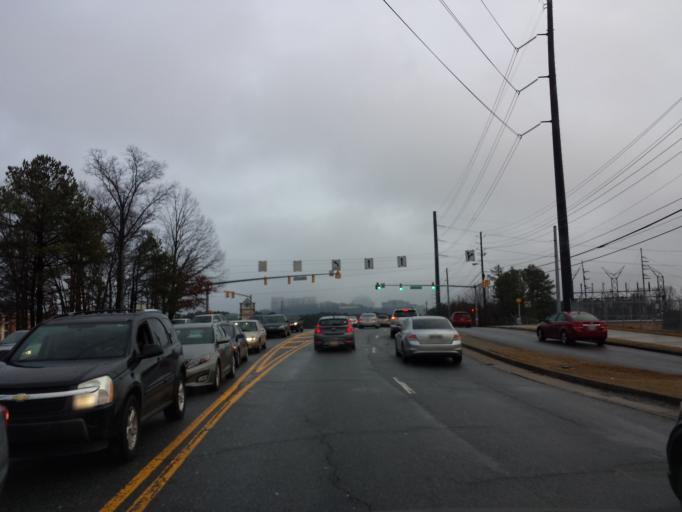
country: US
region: Georgia
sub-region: Cobb County
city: Vinings
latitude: 33.8833
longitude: -84.4756
